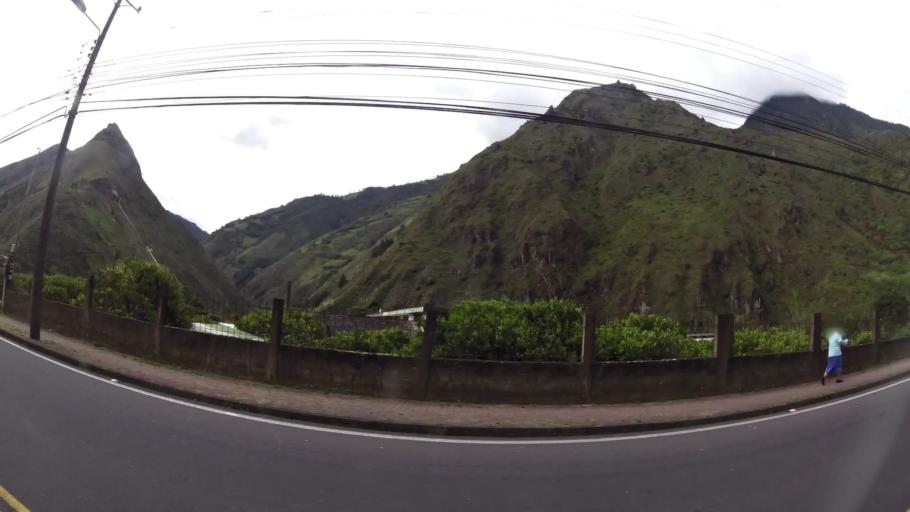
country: EC
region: Tungurahua
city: Banos
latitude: -1.3951
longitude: -78.3894
